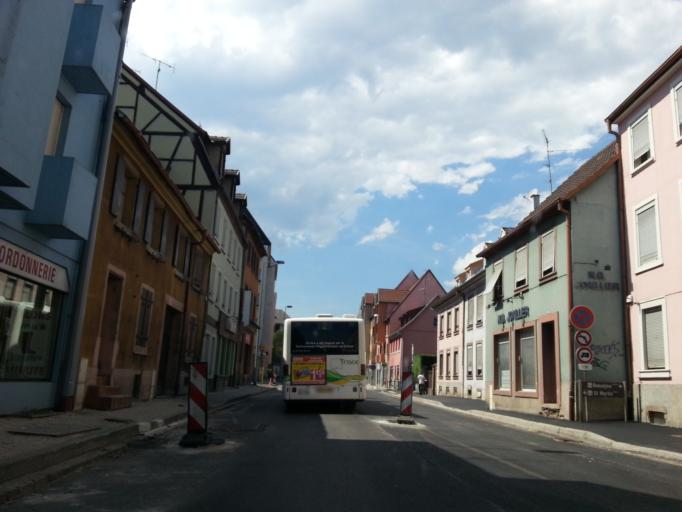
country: FR
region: Alsace
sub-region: Departement du Haut-Rhin
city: Colmar
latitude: 48.0800
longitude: 7.3615
